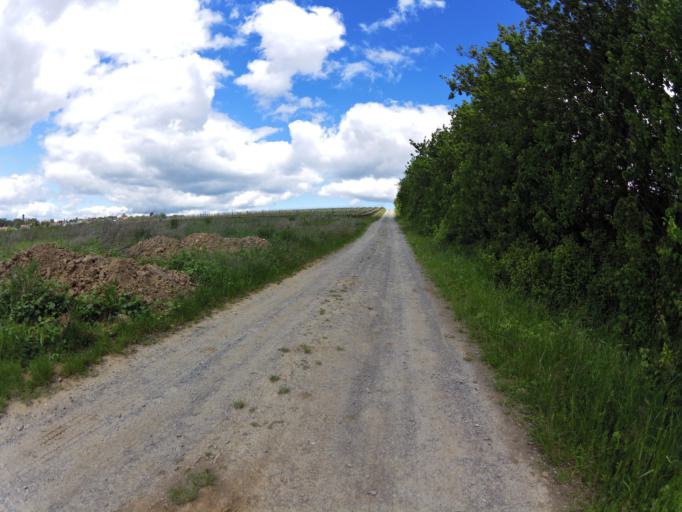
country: DE
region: Bavaria
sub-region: Regierungsbezirk Unterfranken
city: Volkach
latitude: 49.8873
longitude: 10.2368
